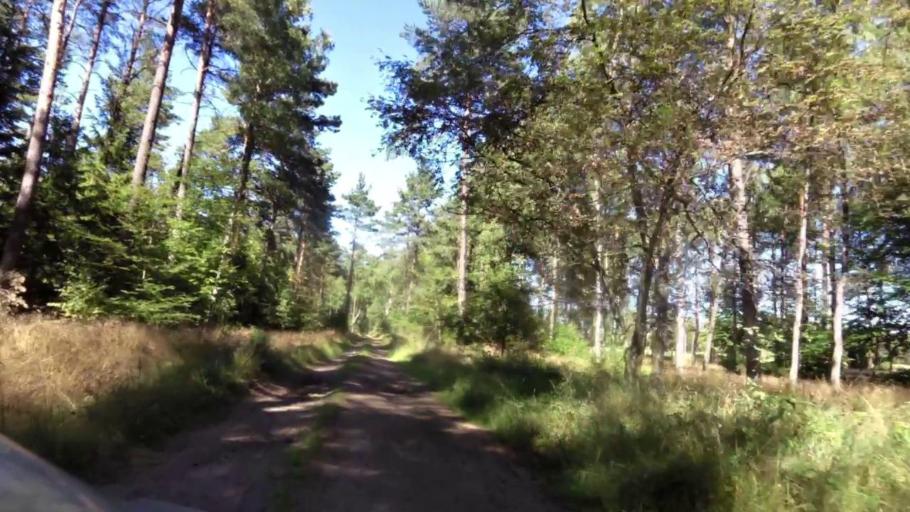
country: PL
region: West Pomeranian Voivodeship
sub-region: Powiat szczecinecki
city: Bialy Bor
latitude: 53.8235
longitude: 16.8663
